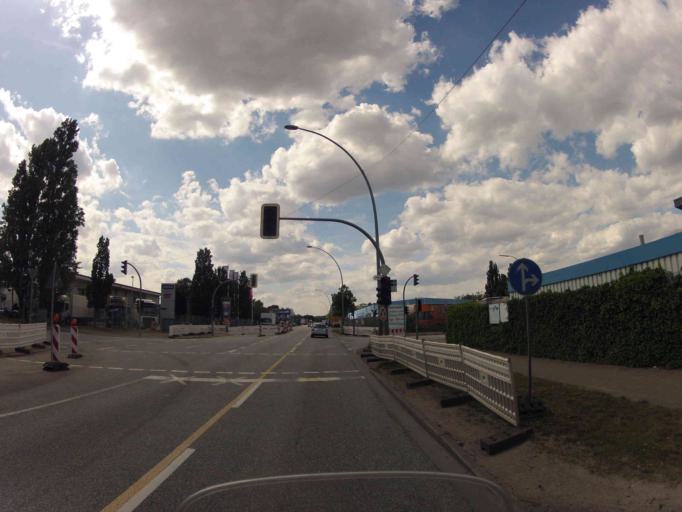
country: DE
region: Hamburg
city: Rothenburgsort
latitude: 53.5377
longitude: 10.0593
